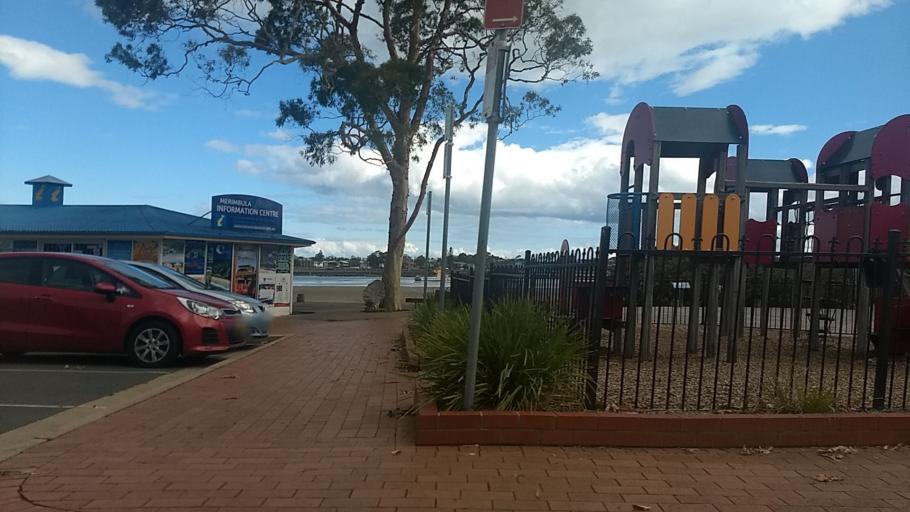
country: AU
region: New South Wales
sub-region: Bega Valley
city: Merimbula
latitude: -36.8888
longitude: 149.9112
